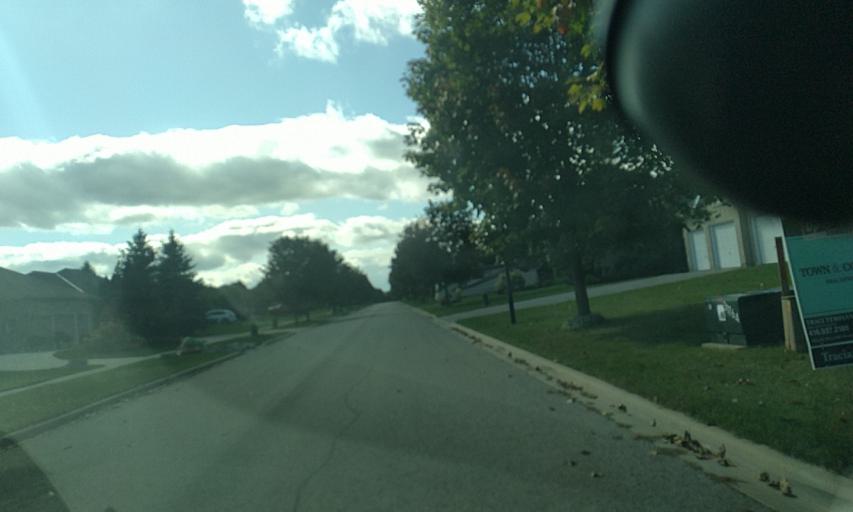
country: CA
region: Ontario
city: Newmarket
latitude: 44.1011
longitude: -79.4251
